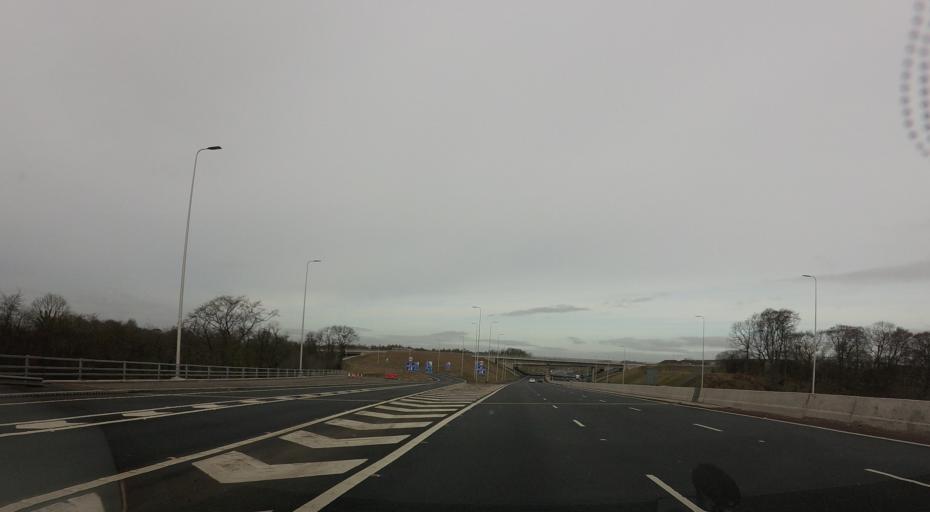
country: GB
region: Scotland
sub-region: North Lanarkshire
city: Bellshill
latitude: 55.8373
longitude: -4.0186
